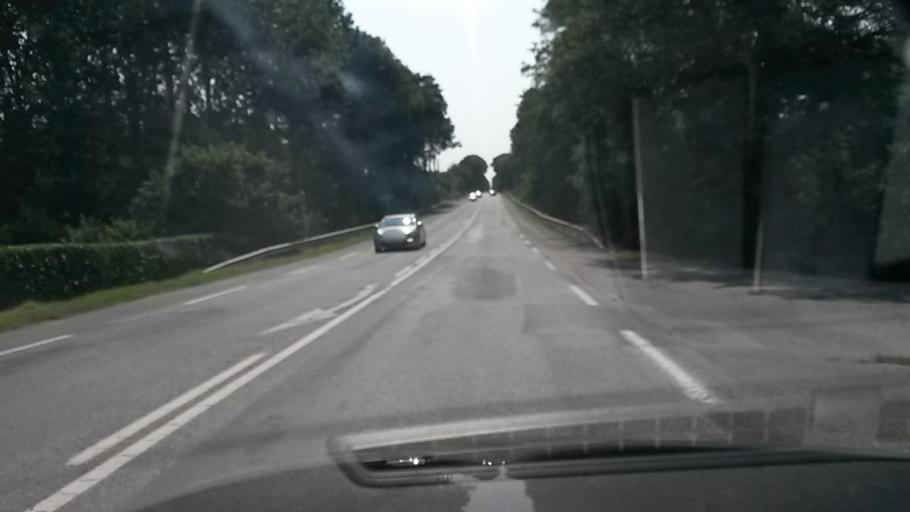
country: FR
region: Pays de la Loire
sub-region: Departement de la Mayenne
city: Chateau-Gontier
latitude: 47.8715
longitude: -0.6872
